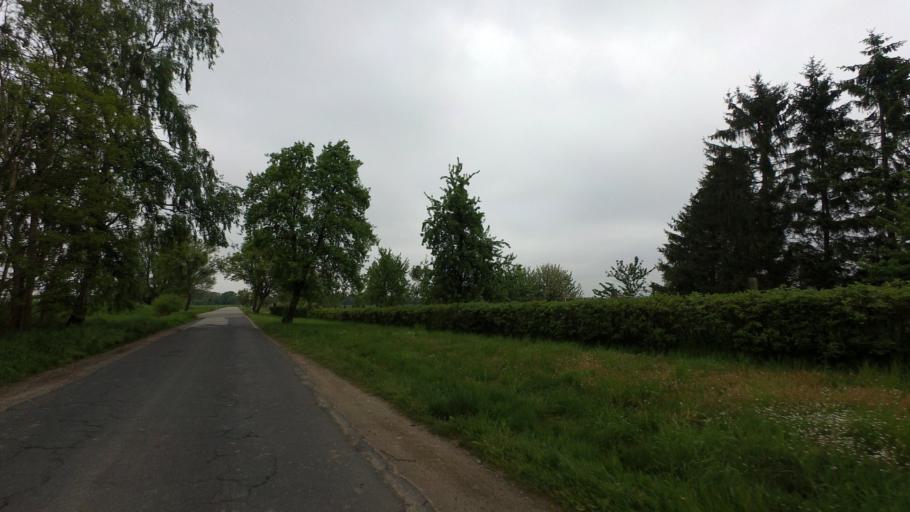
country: DE
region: Mecklenburg-Vorpommern
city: Mollenhagen
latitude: 53.6059
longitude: 12.9244
